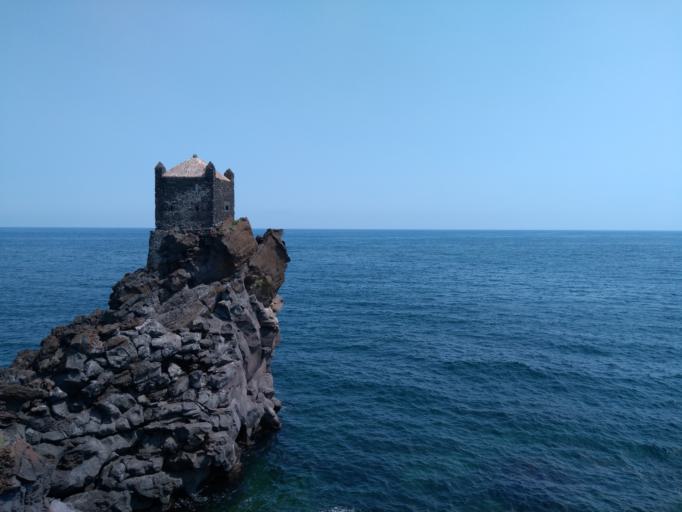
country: IT
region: Sicily
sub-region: Catania
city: Acireale
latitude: 37.6403
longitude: 15.1840
